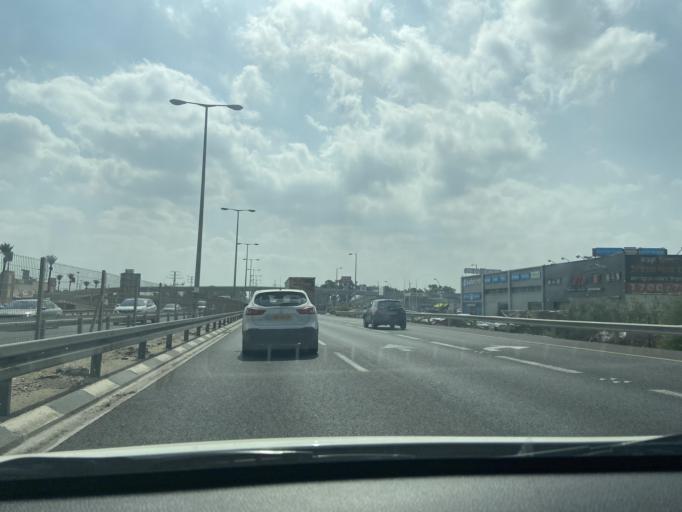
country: IL
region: Northern District
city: `Akko
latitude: 32.9015
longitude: 35.0908
